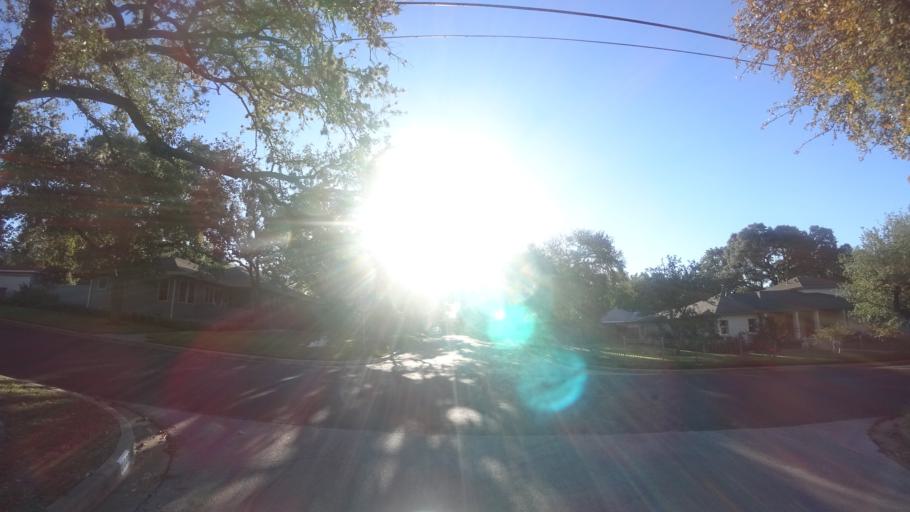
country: US
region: Texas
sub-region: Travis County
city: West Lake Hills
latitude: 30.2968
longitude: -97.7785
